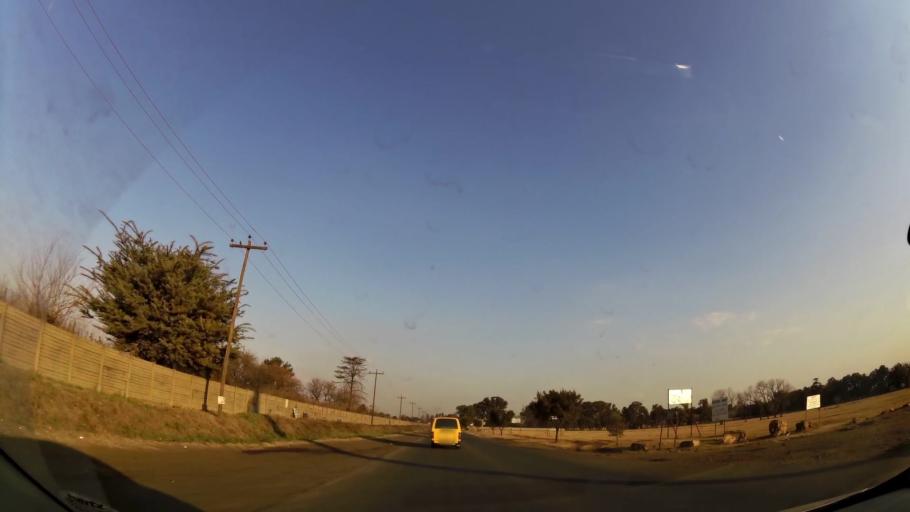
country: ZA
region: Gauteng
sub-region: Ekurhuleni Metropolitan Municipality
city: Germiston
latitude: -26.2915
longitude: 28.2300
